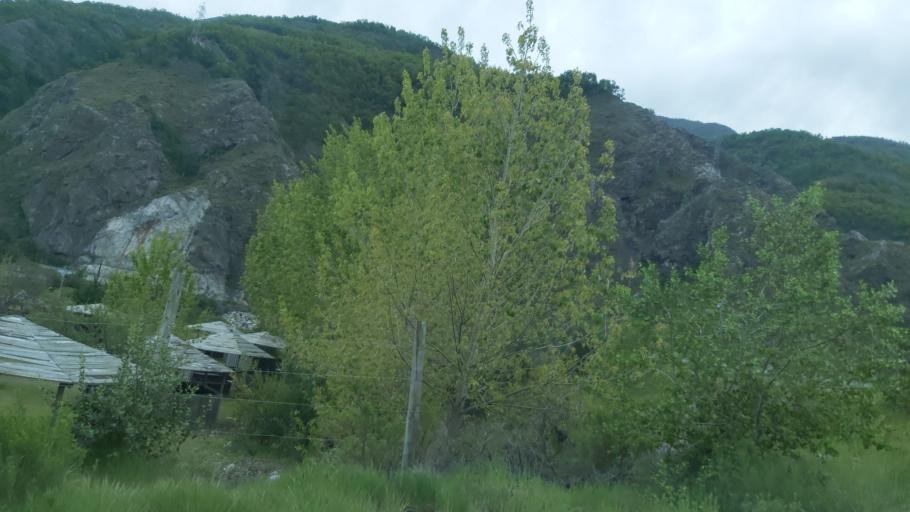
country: CL
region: Maule
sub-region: Provincia de Linares
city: Colbun
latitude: -35.7147
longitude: -71.1219
